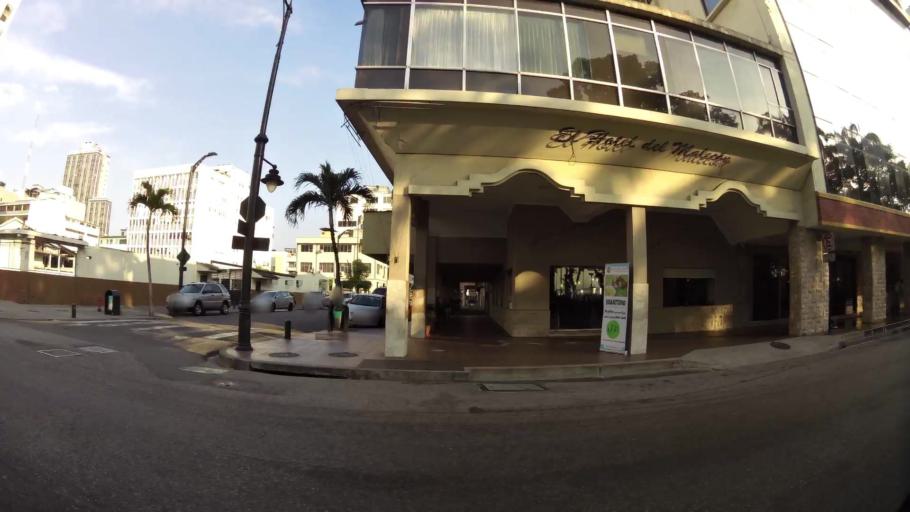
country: EC
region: Guayas
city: Eloy Alfaro
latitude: -2.1888
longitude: -79.8784
